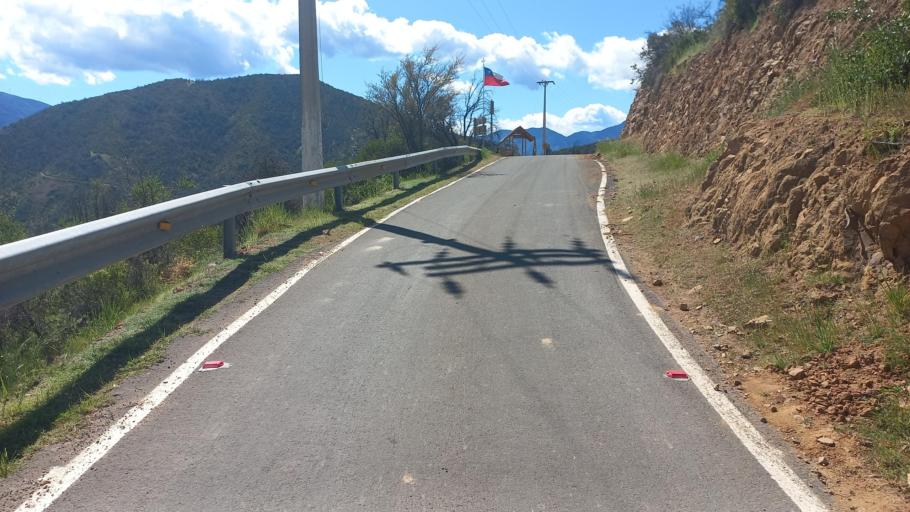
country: CL
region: Santiago Metropolitan
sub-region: Provincia de Chacabuco
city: Lampa
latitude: -33.1937
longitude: -71.0915
